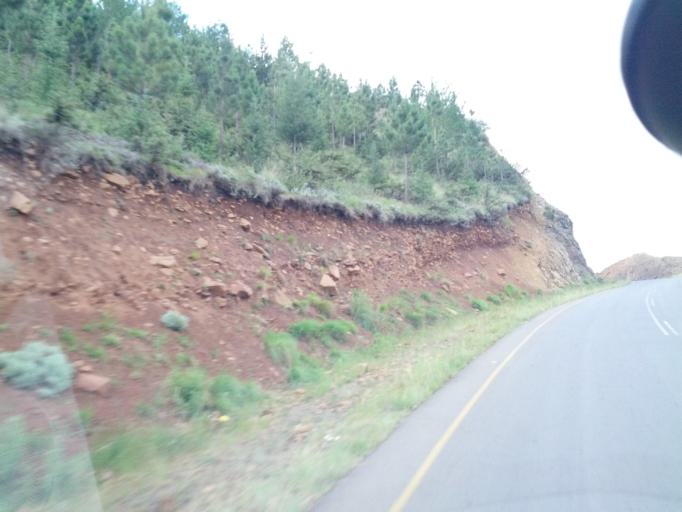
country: LS
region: Qacha's Nek
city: Qacha's Nek
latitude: -30.0769
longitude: 28.6210
